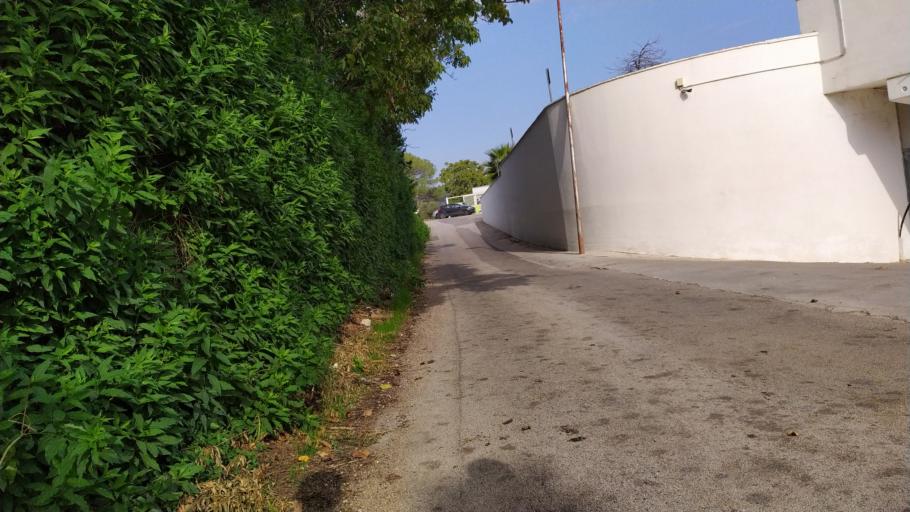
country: IT
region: Campania
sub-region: Provincia di Caserta
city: Maddaloni
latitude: 41.0289
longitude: 14.3963
